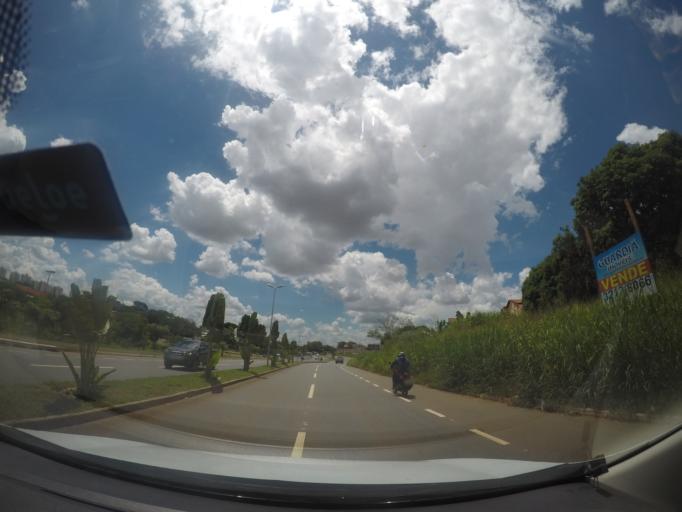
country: BR
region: Goias
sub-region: Goiania
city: Goiania
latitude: -16.7104
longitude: -49.3174
